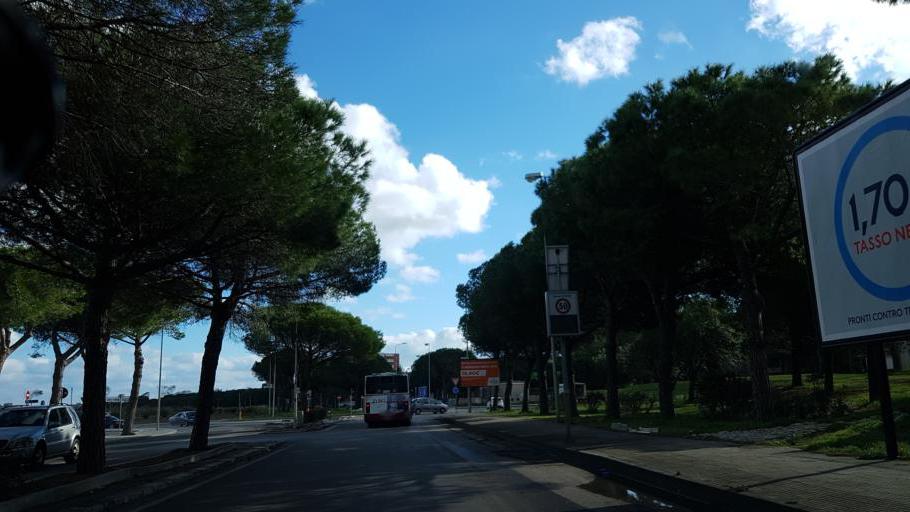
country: IT
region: Apulia
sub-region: Provincia di Brindisi
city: Brindisi
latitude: 40.6214
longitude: 17.9172
